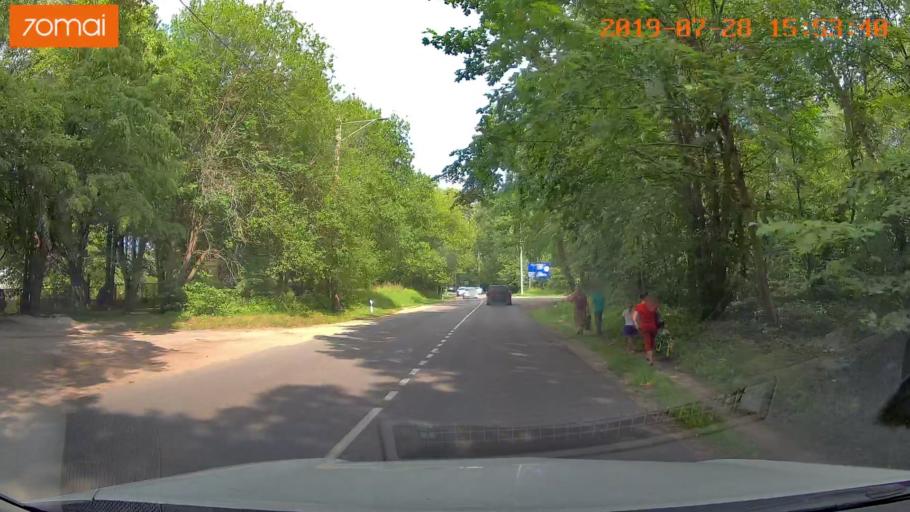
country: RU
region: Kaliningrad
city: Otradnoye
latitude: 54.9397
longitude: 20.1259
